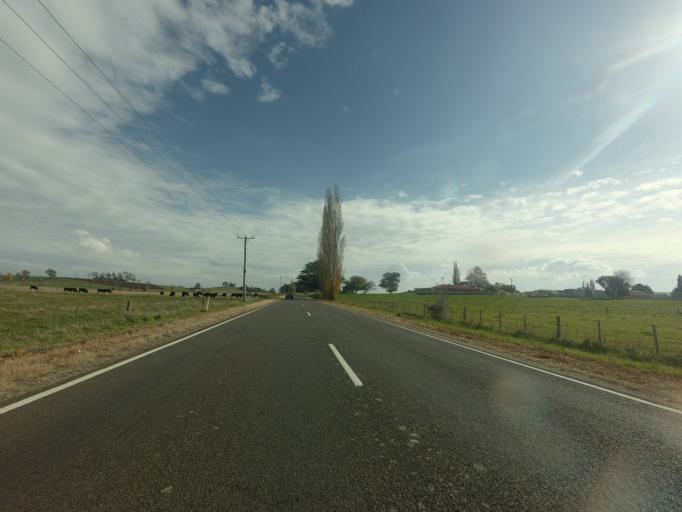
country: AU
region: Tasmania
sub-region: Meander Valley
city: Deloraine
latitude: -41.5249
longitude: 146.7060
